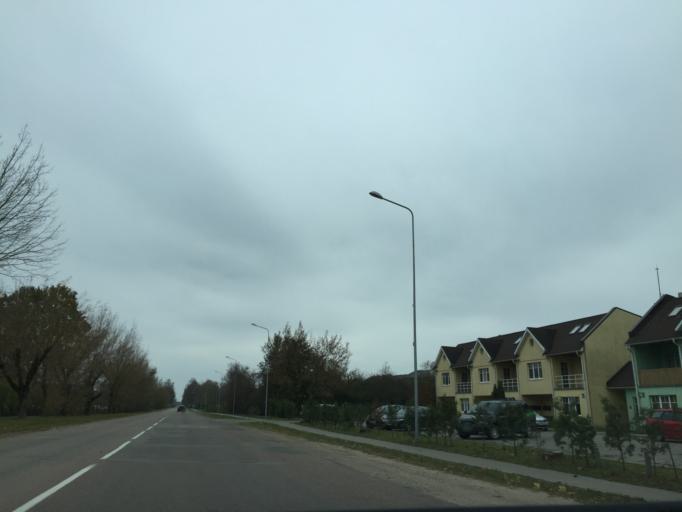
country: LV
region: Marupe
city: Marupe
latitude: 56.8819
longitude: 24.0687
